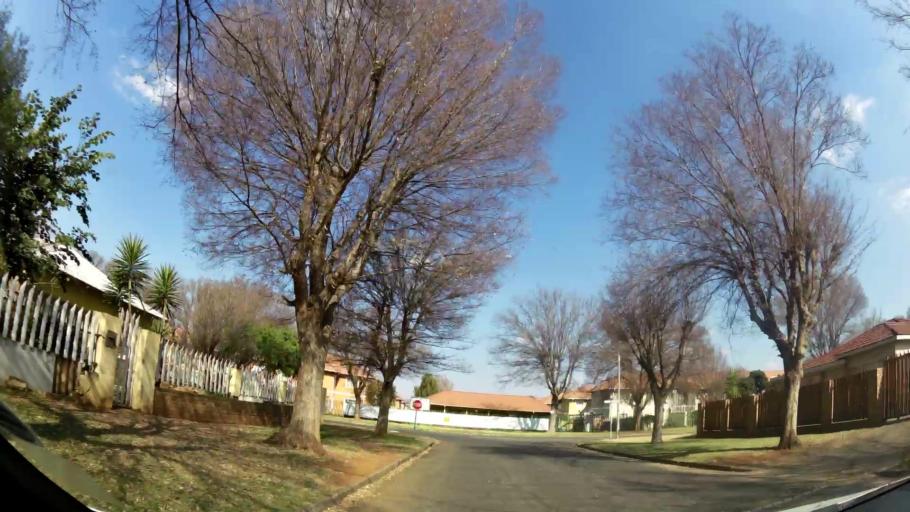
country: ZA
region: Gauteng
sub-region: Ekurhuleni Metropolitan Municipality
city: Boksburg
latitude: -26.2011
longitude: 28.2379
